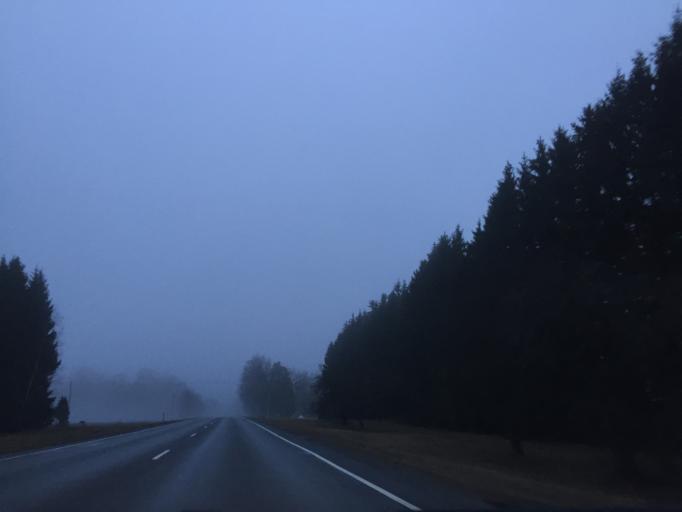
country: EE
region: Laeaene
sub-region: Lihula vald
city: Lihula
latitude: 58.6560
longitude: 23.7202
